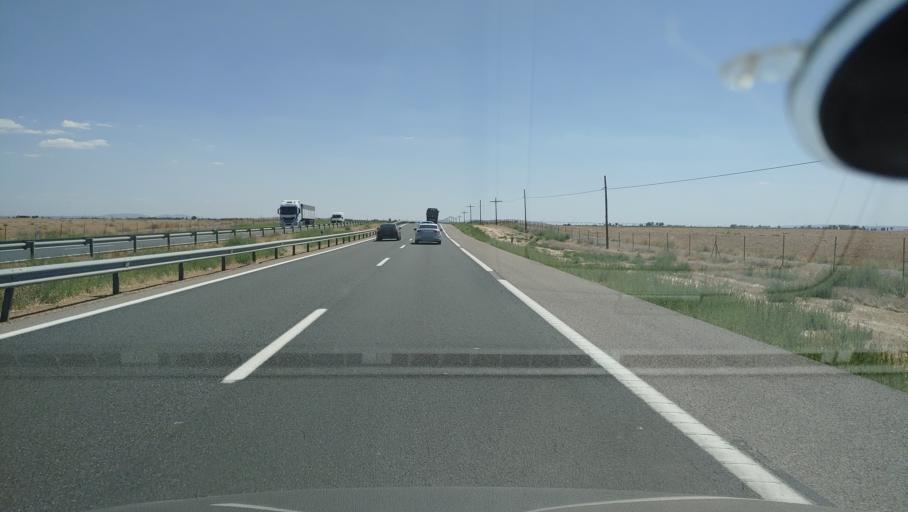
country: ES
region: Castille-La Mancha
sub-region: Provincia de Ciudad Real
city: Villarta de San Juan
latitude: 39.1549
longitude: -3.3886
